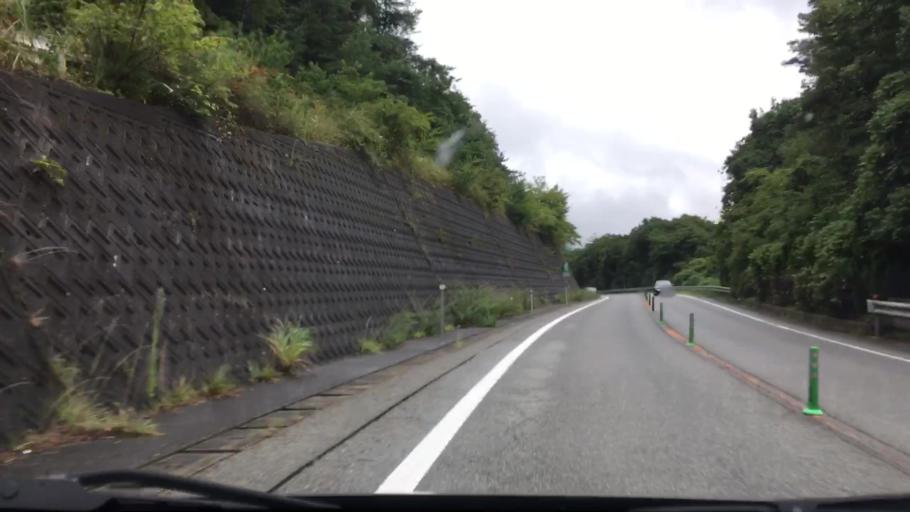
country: JP
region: Hyogo
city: Nishiwaki
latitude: 35.0338
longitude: 134.7685
